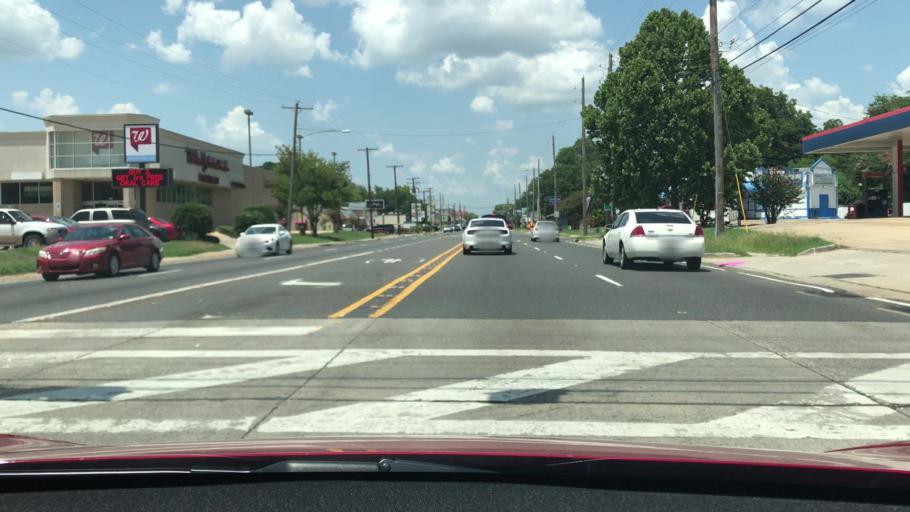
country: US
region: Louisiana
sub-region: Bossier Parish
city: Bossier City
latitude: 32.4568
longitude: -93.7221
